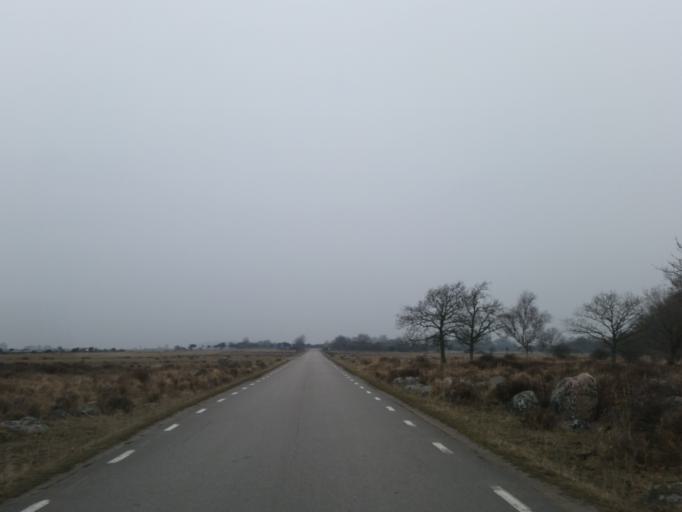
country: SE
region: Kalmar
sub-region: Morbylanga Kommun
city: Moerbylanga
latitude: 56.2130
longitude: 16.4073
